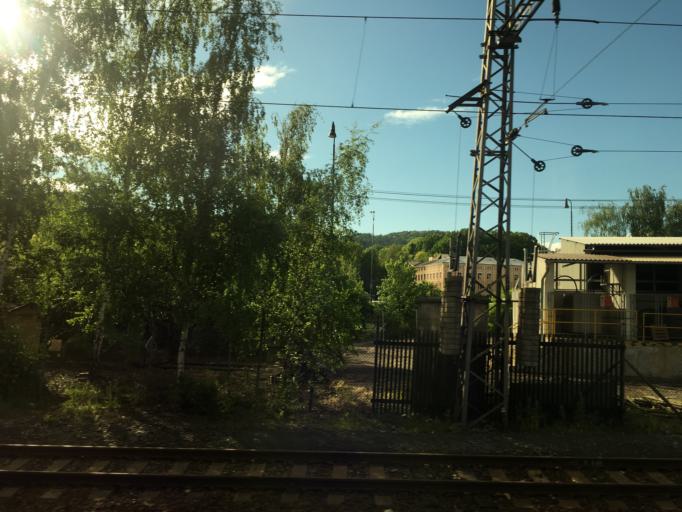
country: CZ
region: Ustecky
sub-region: Okres Decin
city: Decin
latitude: 50.7587
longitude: 14.1943
